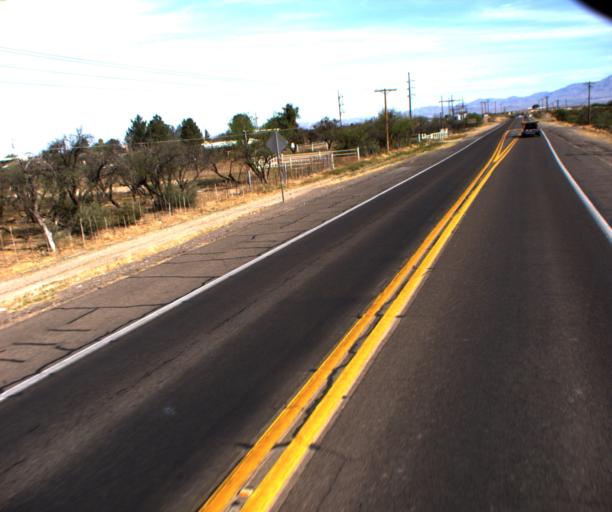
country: US
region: Arizona
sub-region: Graham County
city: Cactus Flat
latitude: 32.7718
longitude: -109.7163
